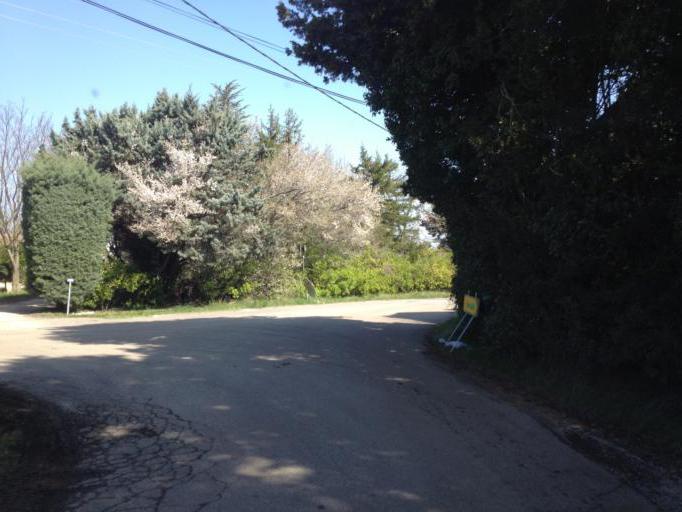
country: FR
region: Provence-Alpes-Cote d'Azur
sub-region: Departement du Vaucluse
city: Jonquieres
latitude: 44.1244
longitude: 4.9125
